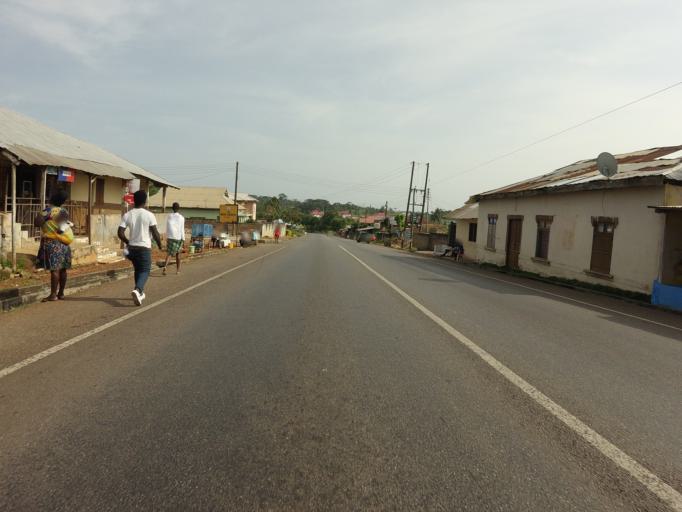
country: GH
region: Eastern
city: Aburi
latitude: 5.8940
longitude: -0.1512
